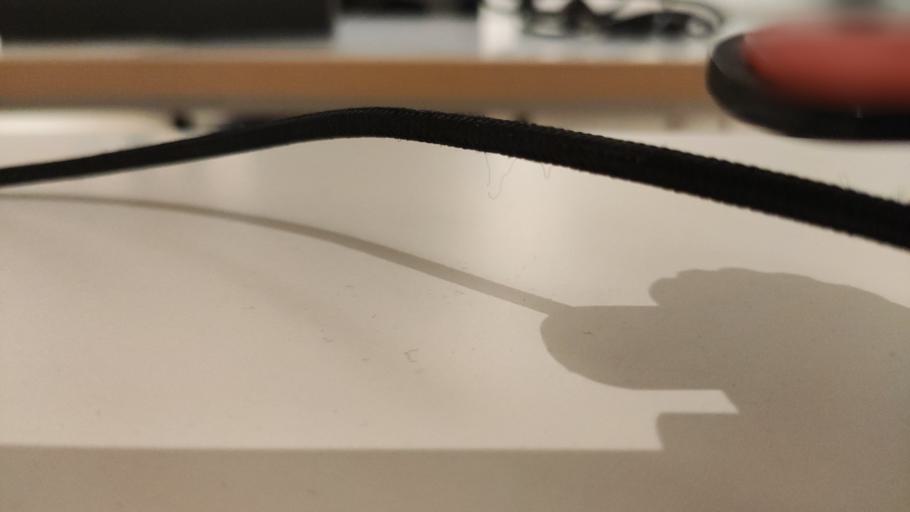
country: RU
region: Moskovskaya
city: Dorokhovo
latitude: 55.4551
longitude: 36.3531
